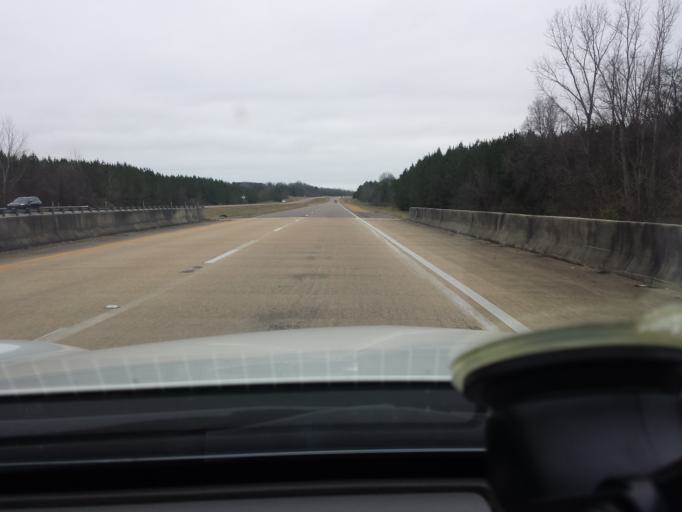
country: US
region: Mississippi
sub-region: Lee County
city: Shannon
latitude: 34.0970
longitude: -88.7006
